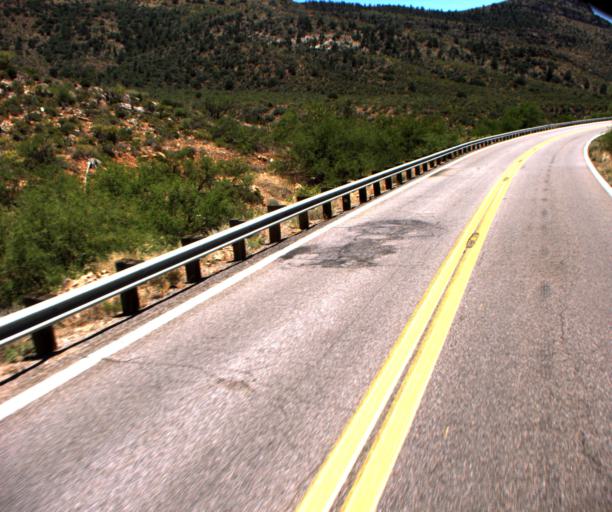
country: US
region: Arizona
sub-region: Pinal County
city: Kearny
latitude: 33.1986
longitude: -110.8041
